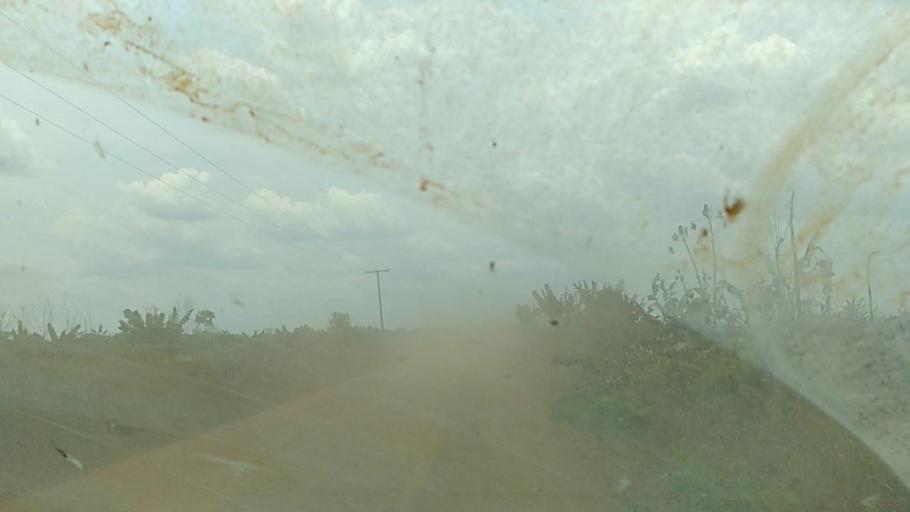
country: BR
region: Rondonia
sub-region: Porto Velho
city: Porto Velho
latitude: -8.9517
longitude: -64.3153
